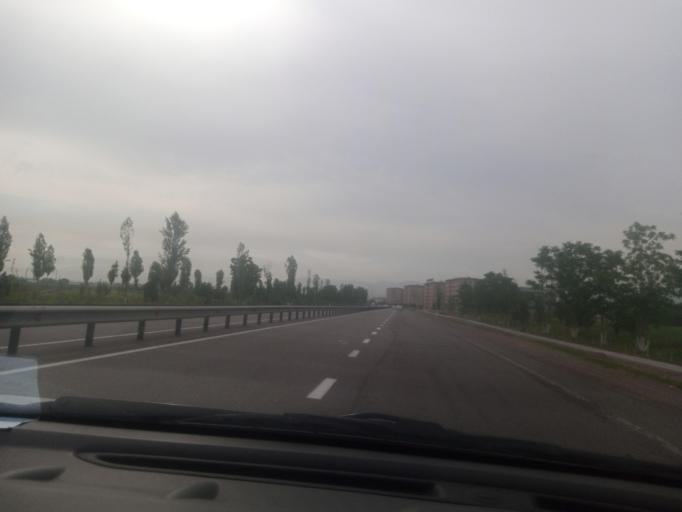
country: UZ
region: Toshkent
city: Ohangaron
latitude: 40.9167
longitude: 69.6044
